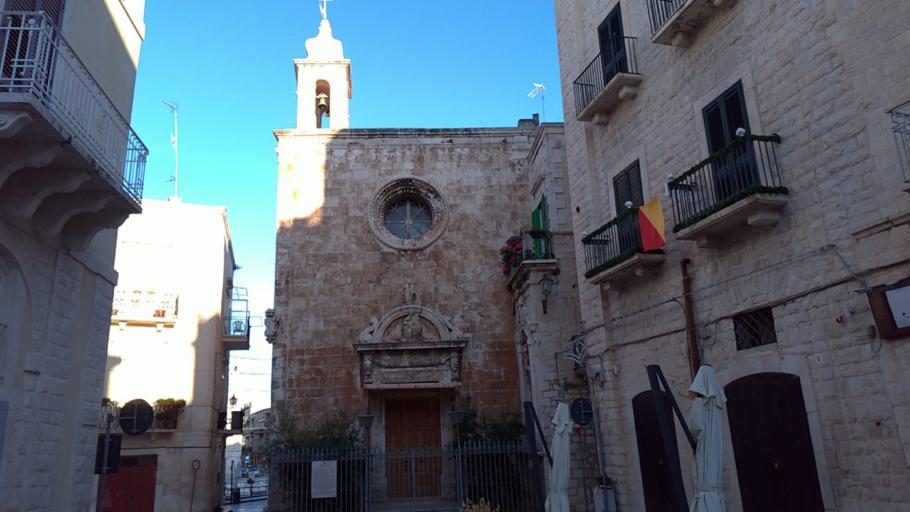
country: IT
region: Apulia
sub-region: Provincia di Bari
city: Giovinazzo
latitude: 41.1885
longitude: 16.6731
